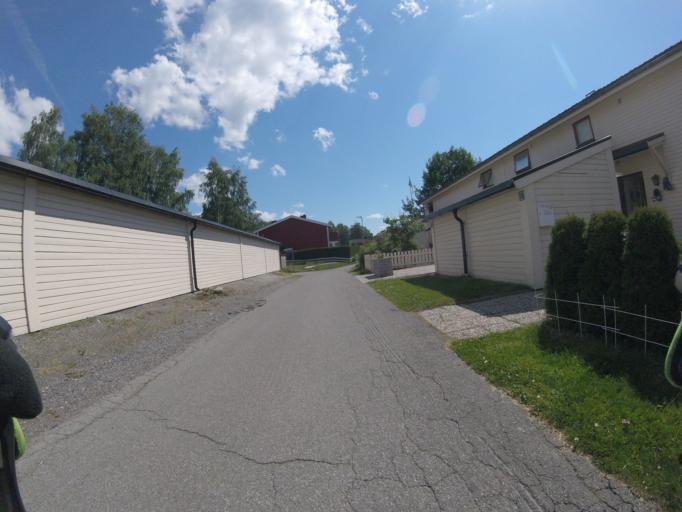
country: NO
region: Akershus
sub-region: Skedsmo
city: Lillestrom
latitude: 59.9528
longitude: 11.0551
